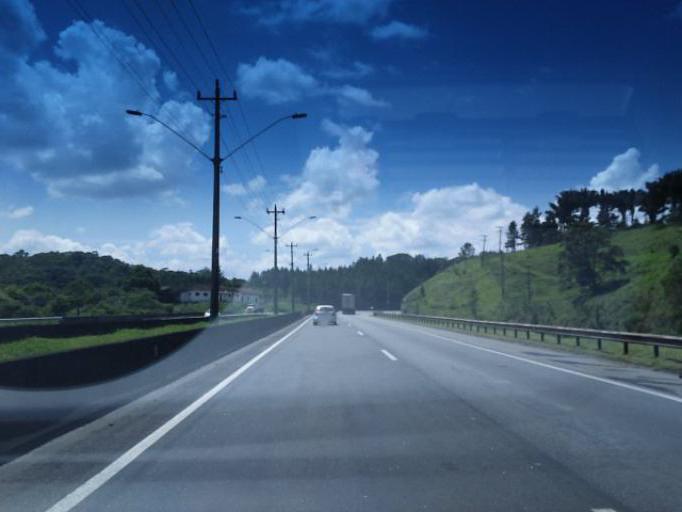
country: BR
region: Sao Paulo
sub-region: Sao Lourenco Da Serra
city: Sao Lourenco da Serra
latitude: -23.9127
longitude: -46.9905
